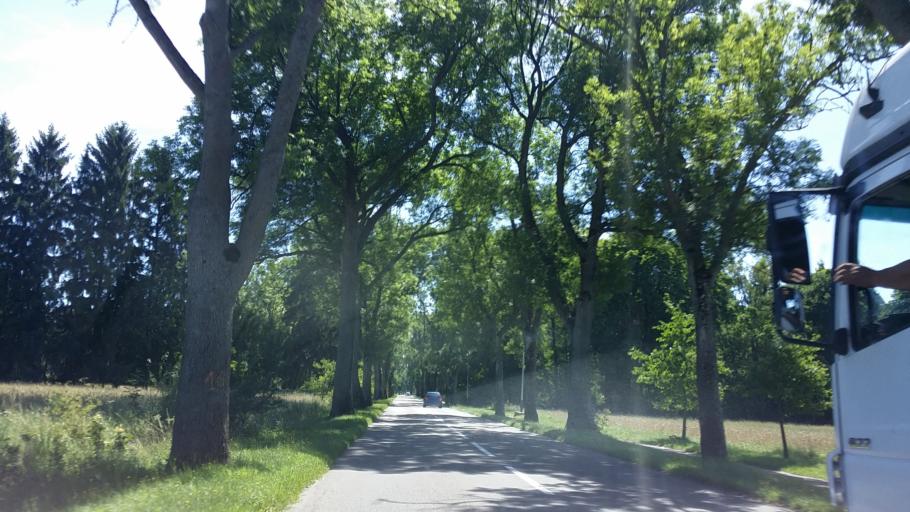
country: PL
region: West Pomeranian Voivodeship
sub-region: Powiat lobeski
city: Lobez
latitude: 53.6202
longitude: 15.6121
